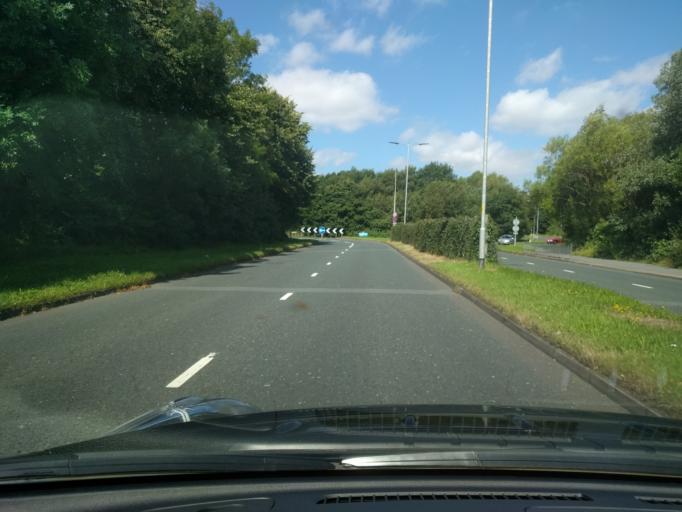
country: GB
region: England
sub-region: Warrington
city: Croft
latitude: 53.4126
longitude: -2.5417
